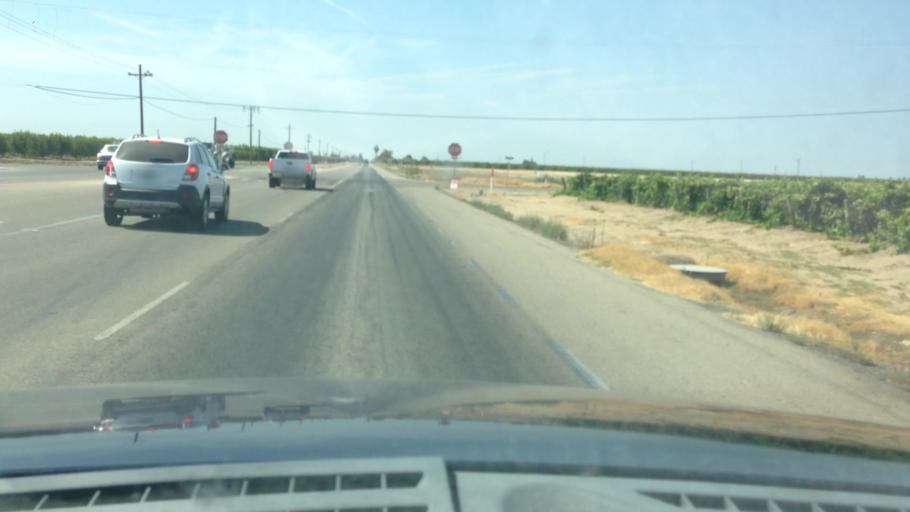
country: US
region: California
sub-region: Fresno County
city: Parlier
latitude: 36.6348
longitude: -119.5568
